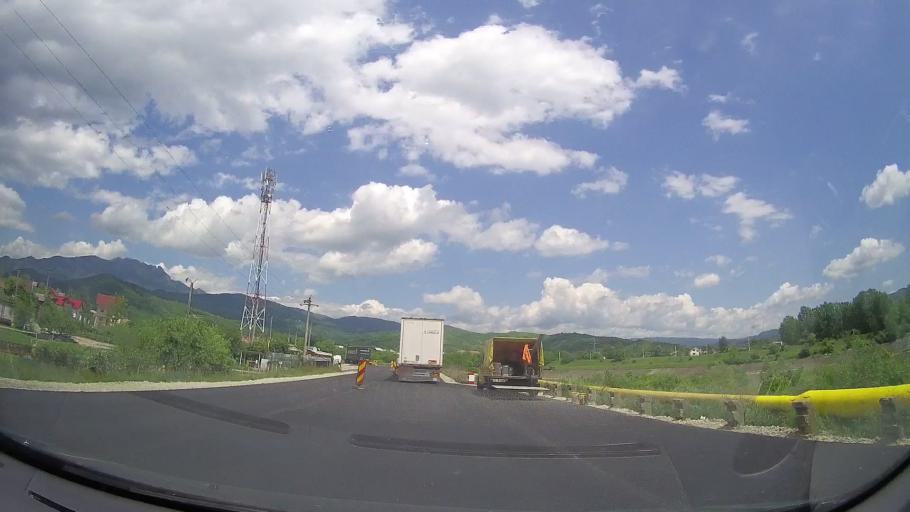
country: RO
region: Valcea
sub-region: Oras Calimanesti
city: Calimanesti
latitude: 45.2349
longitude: 24.3443
